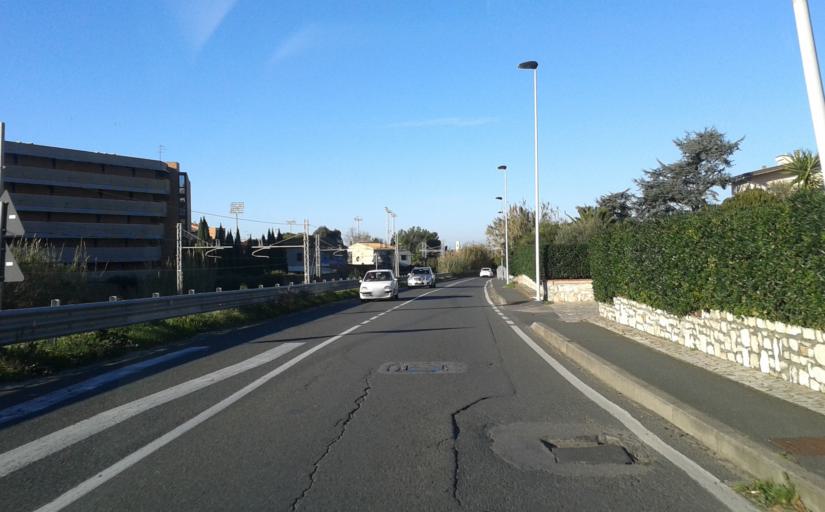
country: IT
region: Tuscany
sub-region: Provincia di Livorno
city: Livorno
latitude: 43.5040
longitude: 10.3275
